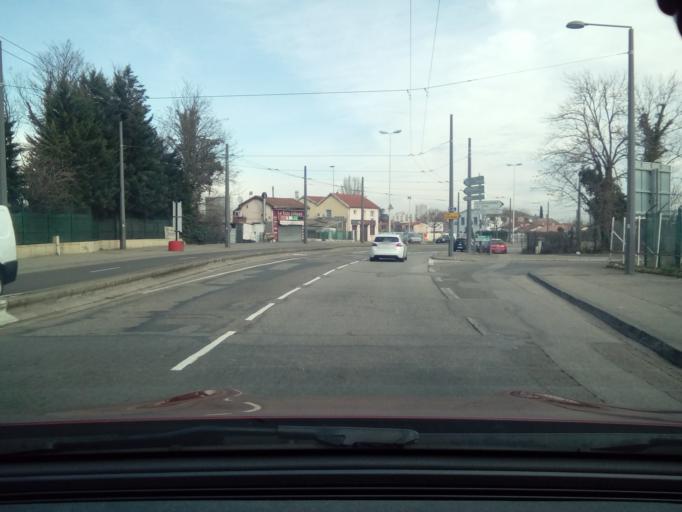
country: FR
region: Rhone-Alpes
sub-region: Departement du Rhone
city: Vaulx-en-Velin
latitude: 45.7703
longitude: 4.9066
